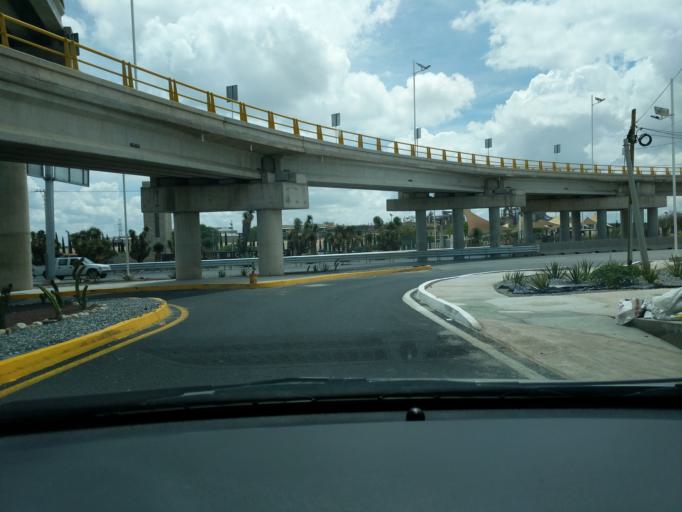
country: MX
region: San Luis Potosi
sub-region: Mexquitic de Carmona
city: Guadalupe Victoria
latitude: 22.1696
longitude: -101.0408
